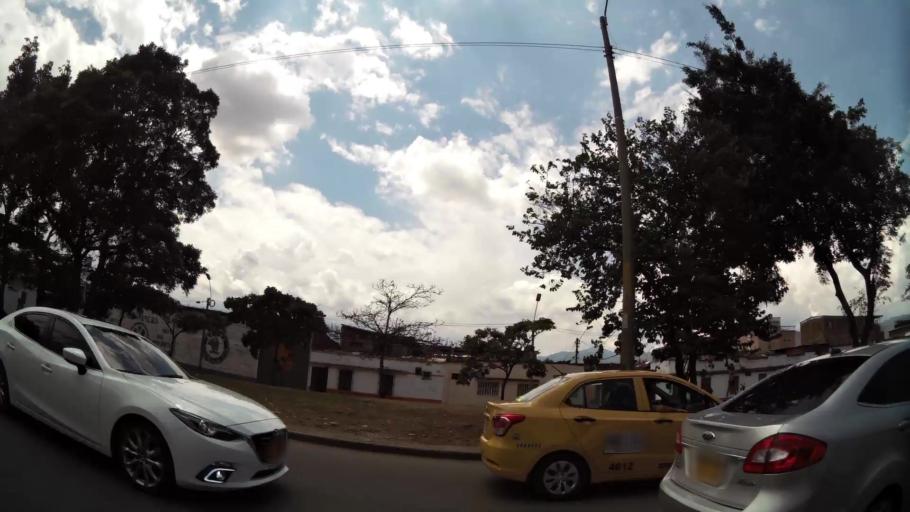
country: CO
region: Valle del Cauca
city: Cali
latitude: 3.4403
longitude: -76.5187
